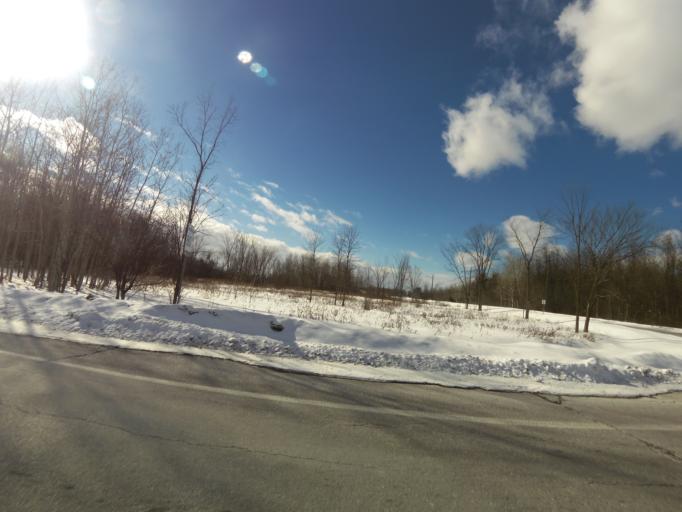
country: CA
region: Ontario
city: Ottawa
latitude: 45.4008
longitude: -75.5844
